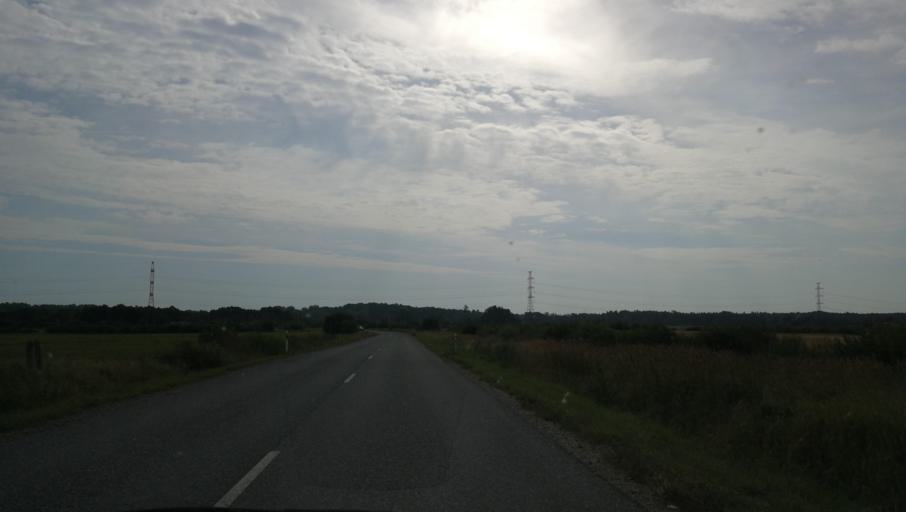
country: LV
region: Alsunga
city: Alsunga
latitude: 56.9854
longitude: 21.5306
